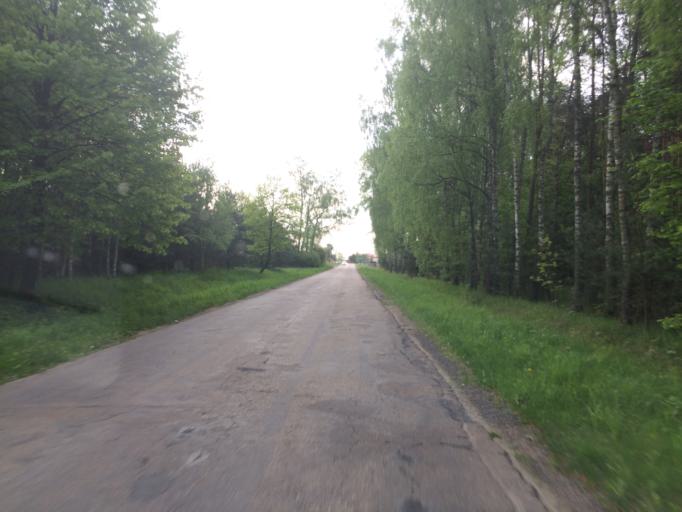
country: PL
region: Warmian-Masurian Voivodeship
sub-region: Powiat dzialdowski
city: Dzialdowo
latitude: 53.2906
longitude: 20.1132
